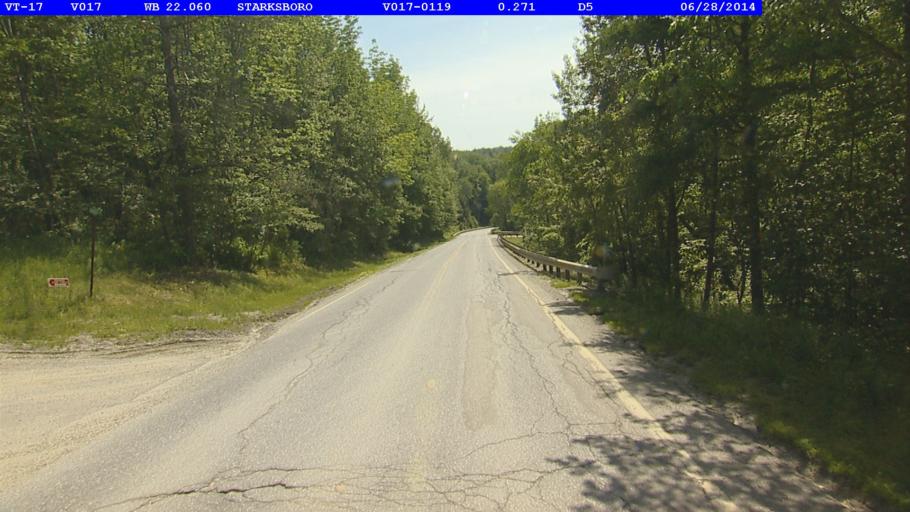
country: US
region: Vermont
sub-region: Addison County
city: Bristol
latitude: 44.1634
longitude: -73.0127
